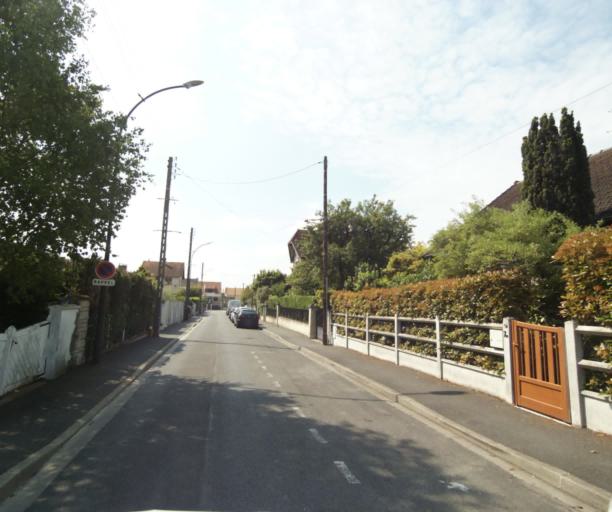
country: FR
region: Ile-de-France
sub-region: Departement du Val-d'Oise
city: Sannois
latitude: 48.9618
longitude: 2.2335
